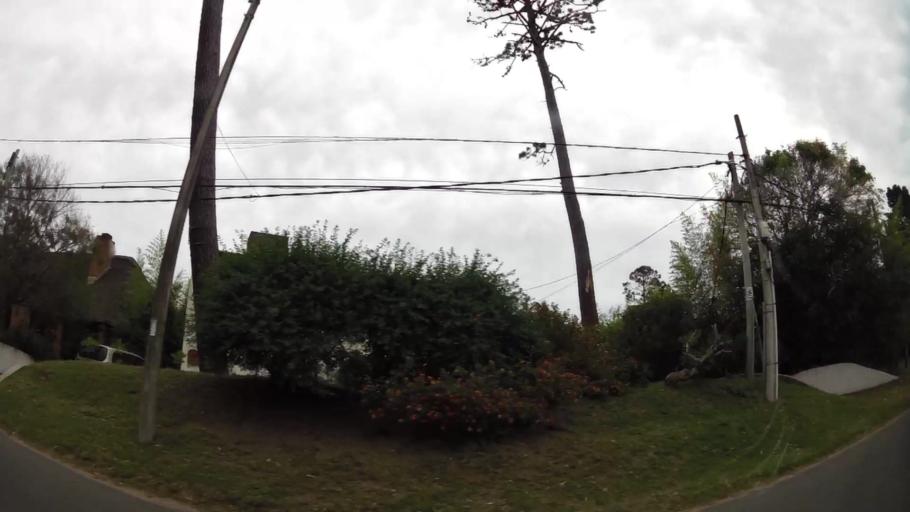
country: UY
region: Maldonado
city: Maldonado
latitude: -34.9087
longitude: -54.9898
